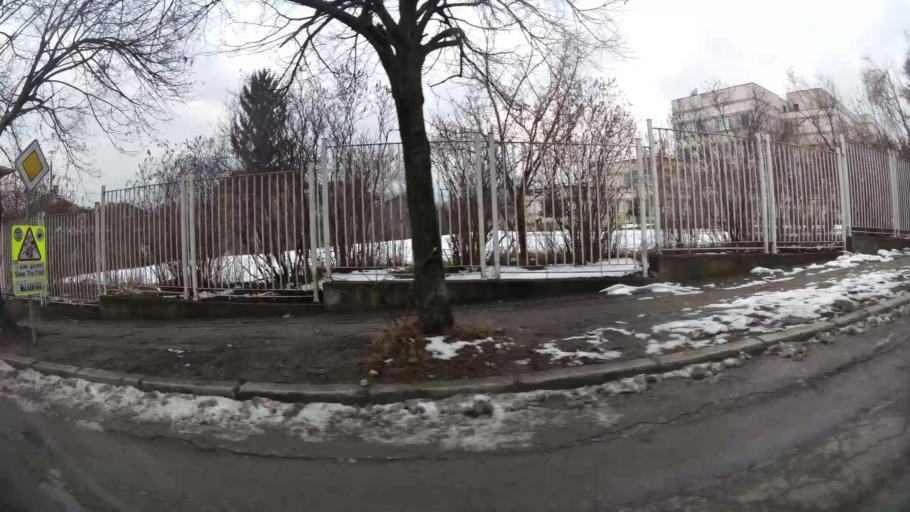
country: BG
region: Sofiya
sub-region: Obshtina Bozhurishte
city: Bozhurishte
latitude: 42.6756
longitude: 23.2334
